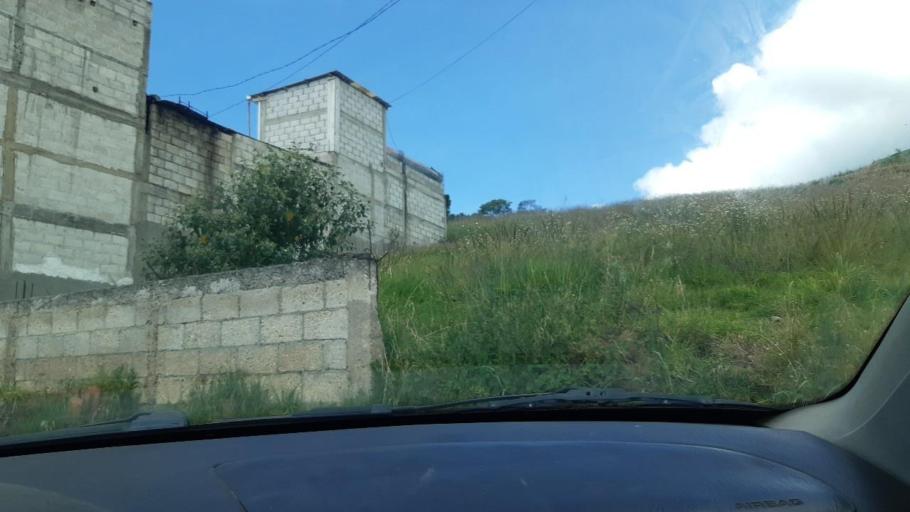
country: GT
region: Quetzaltenango
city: Salcaja
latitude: 14.8799
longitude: -91.4636
